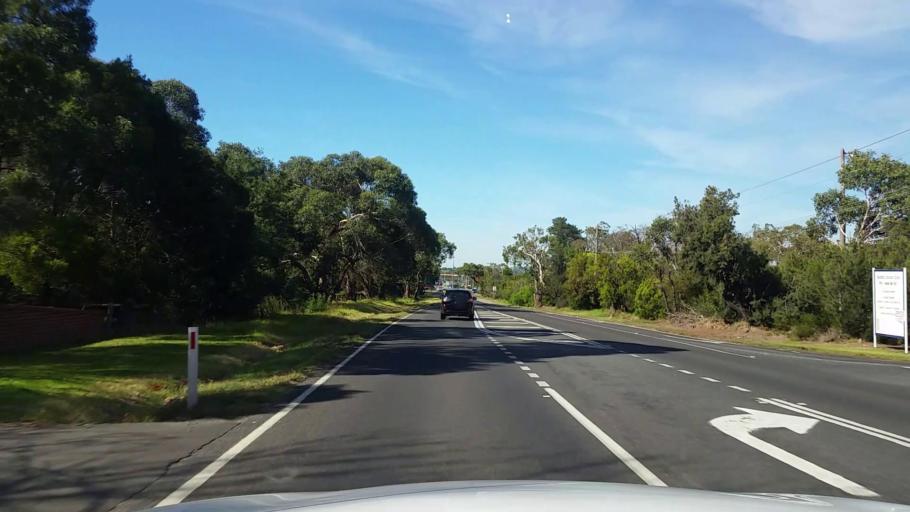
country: AU
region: Victoria
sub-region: Mornington Peninsula
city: Baxter
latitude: -38.1915
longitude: 145.1466
